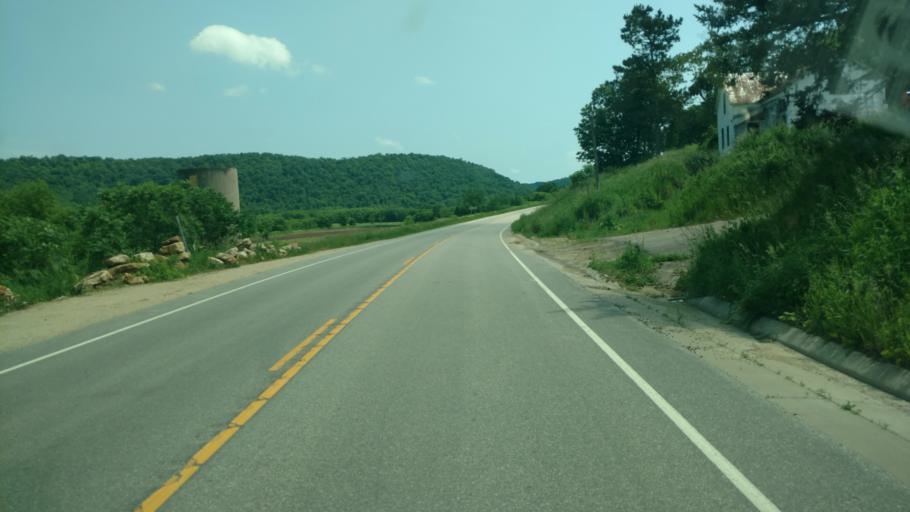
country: US
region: Wisconsin
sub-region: Vernon County
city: Viroqua
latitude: 43.5150
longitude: -90.6609
